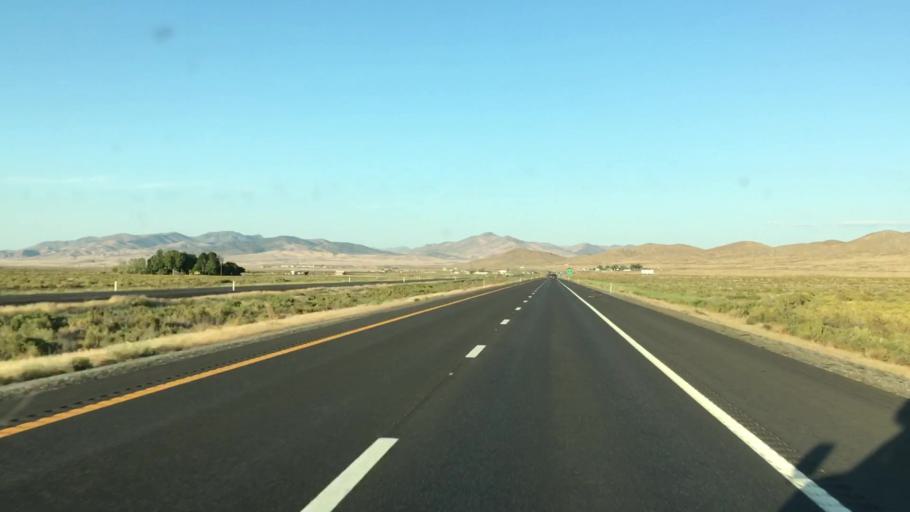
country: US
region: Nevada
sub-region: Humboldt County
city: Winnemucca
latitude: 40.6701
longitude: -118.0990
